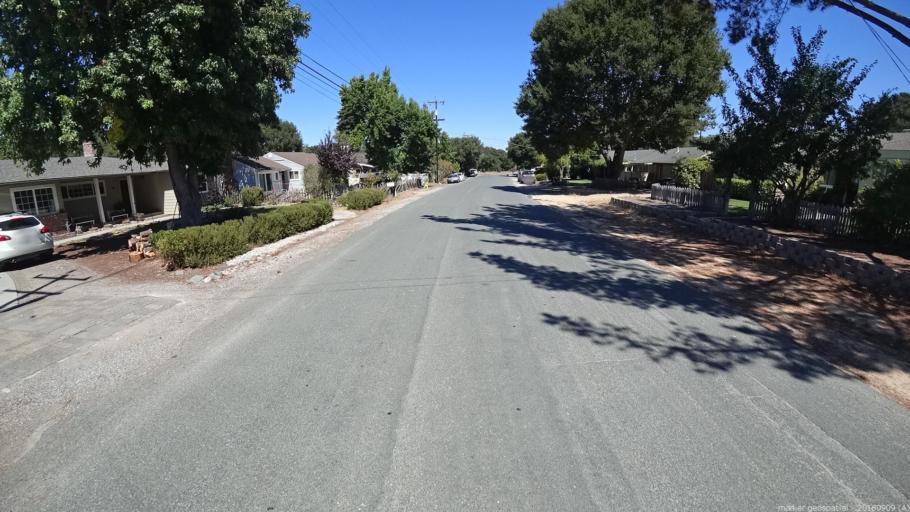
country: US
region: California
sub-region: Monterey County
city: Carmel Valley Village
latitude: 36.5775
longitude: -121.7203
